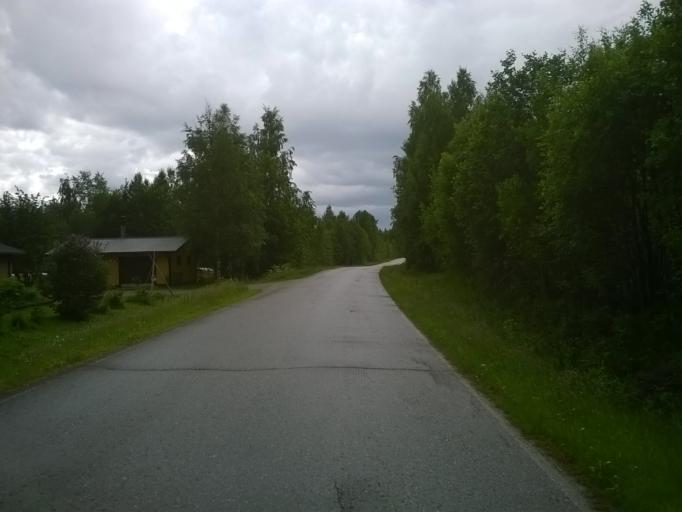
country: FI
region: Kainuu
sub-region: Kehys-Kainuu
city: Kuhmo
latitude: 64.1334
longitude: 29.4056
